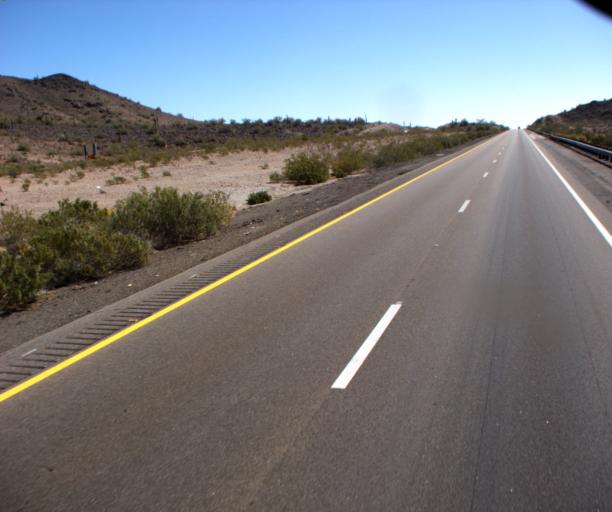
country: US
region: Arizona
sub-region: La Paz County
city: Salome
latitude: 33.6110
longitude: -113.6347
